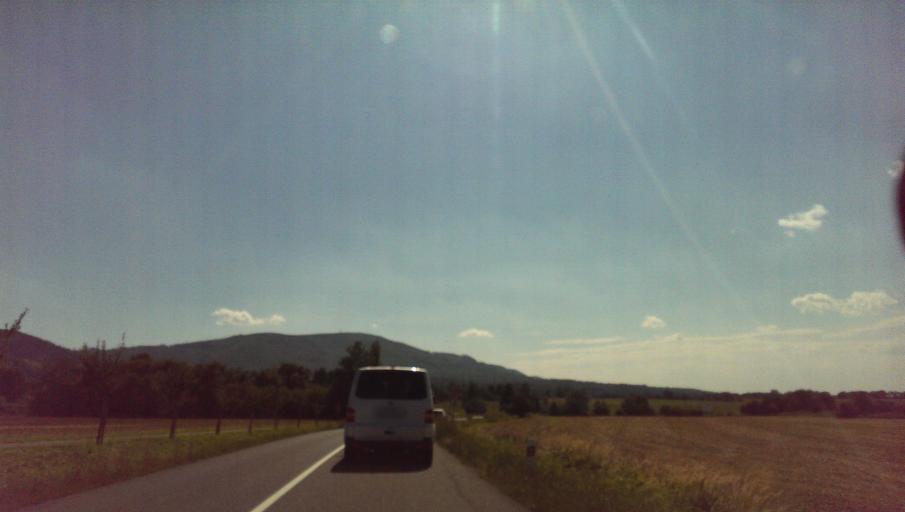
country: CZ
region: Zlin
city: Kelc
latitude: 49.4357
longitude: 17.8027
